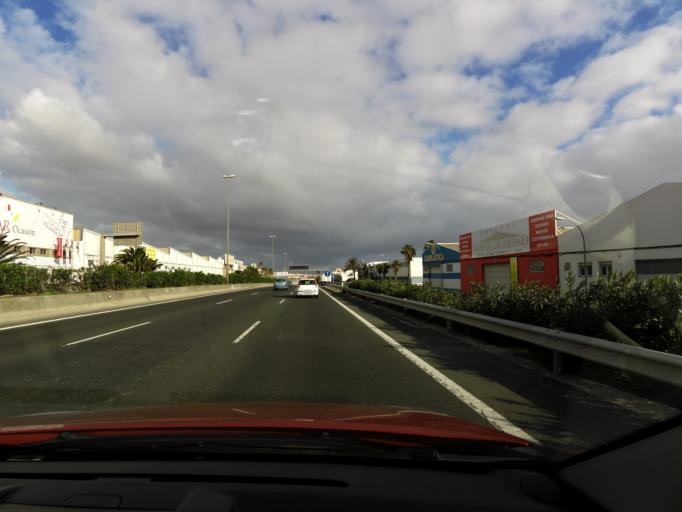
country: ES
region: Canary Islands
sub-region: Provincia de Las Palmas
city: Telde
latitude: 27.9698
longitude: -15.3906
